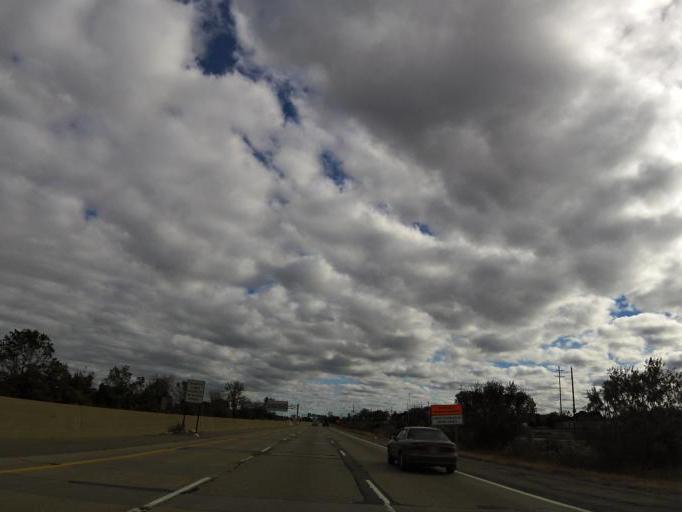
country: US
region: Michigan
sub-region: Genesee County
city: Flint
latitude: 42.9895
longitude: -83.7162
